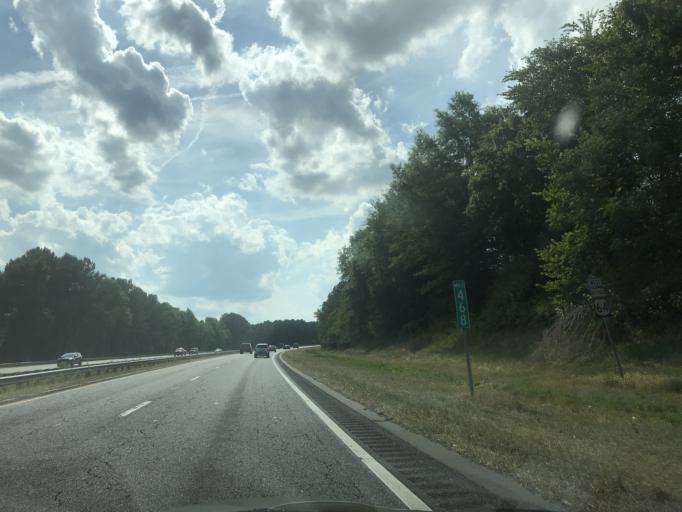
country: US
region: North Carolina
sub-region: Nash County
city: Rocky Mount
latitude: 35.9645
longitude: -77.8108
